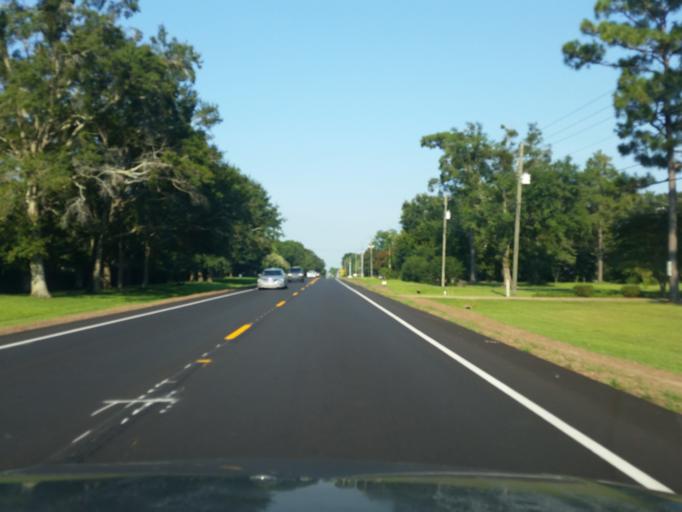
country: US
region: Alabama
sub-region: Baldwin County
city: Foley
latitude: 30.4066
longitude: -87.7481
